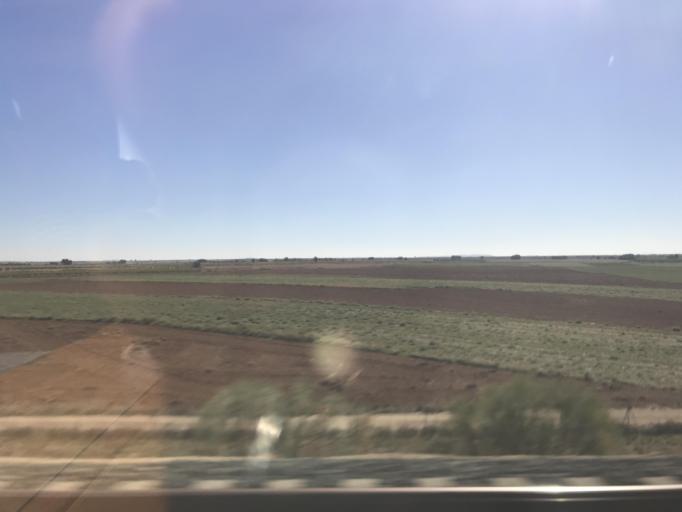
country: ES
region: Castille-La Mancha
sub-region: Province of Toledo
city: Noblejas
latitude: 39.9463
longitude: -3.4085
